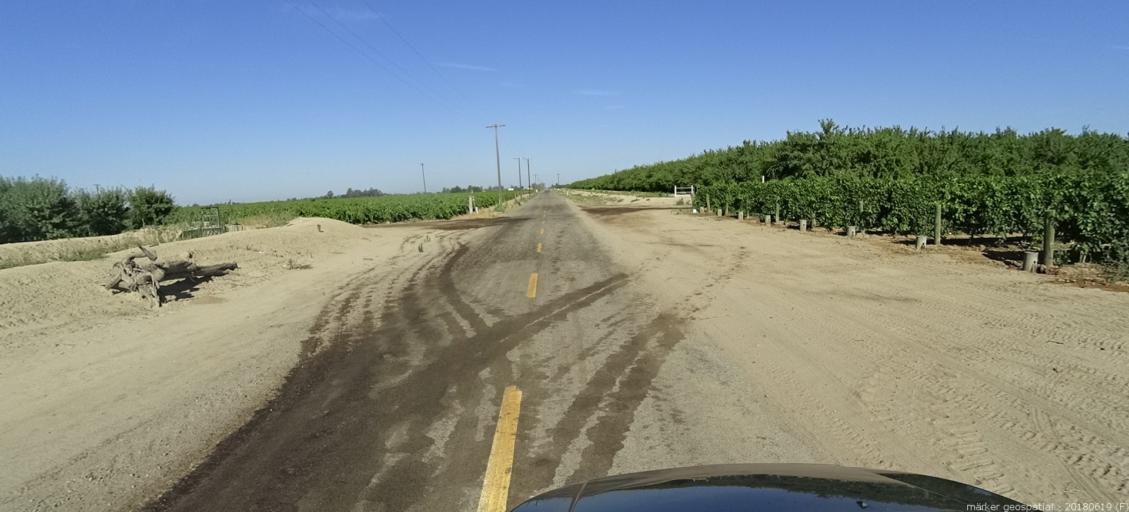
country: US
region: California
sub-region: Fresno County
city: Biola
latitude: 36.8296
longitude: -120.0331
